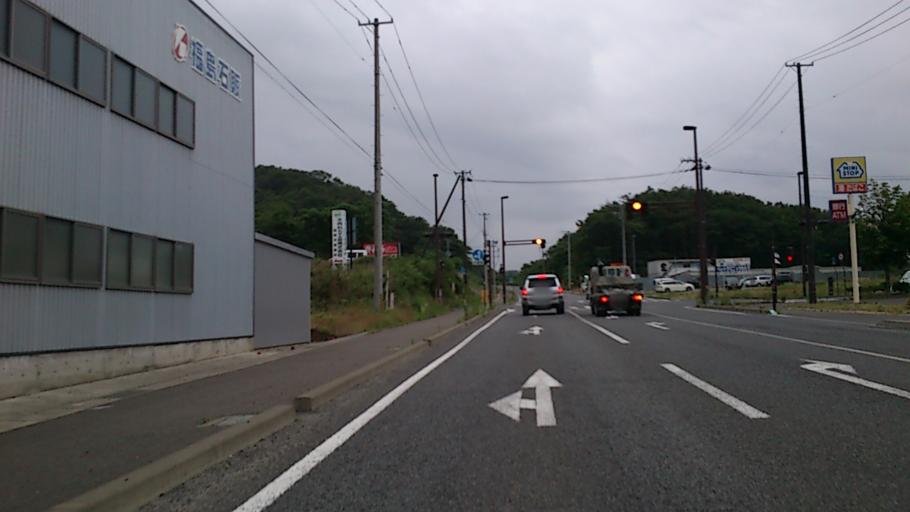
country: JP
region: Fukushima
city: Fukushima-shi
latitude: 37.7254
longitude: 140.4865
